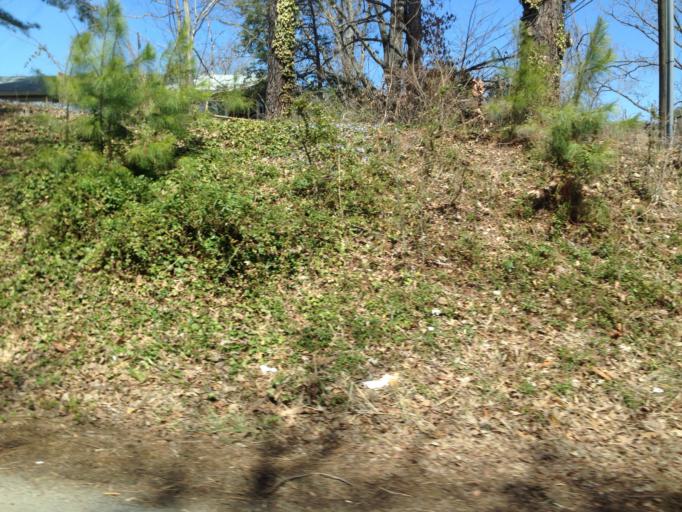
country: US
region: Virginia
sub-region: City of Charlottesville
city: Charlottesville
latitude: 38.0262
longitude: -78.5207
